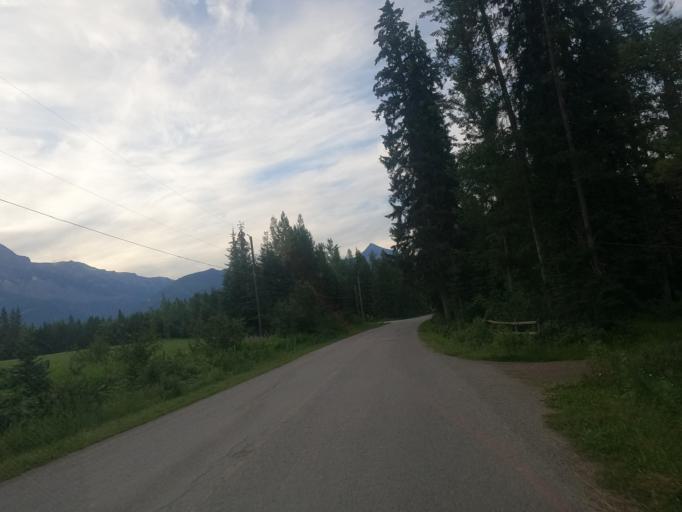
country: CA
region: British Columbia
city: Golden
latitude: 51.4318
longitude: -117.0476
